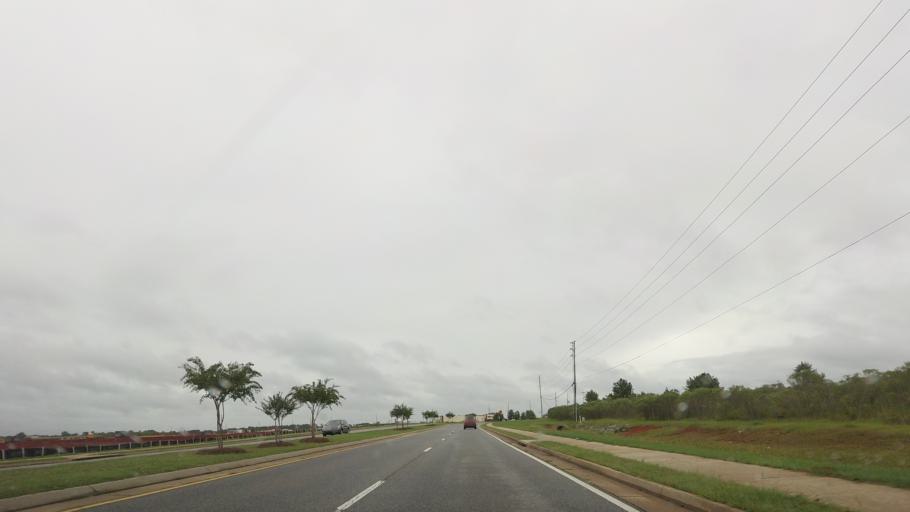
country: US
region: Georgia
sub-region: Houston County
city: Centerville
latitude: 32.5507
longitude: -83.6611
